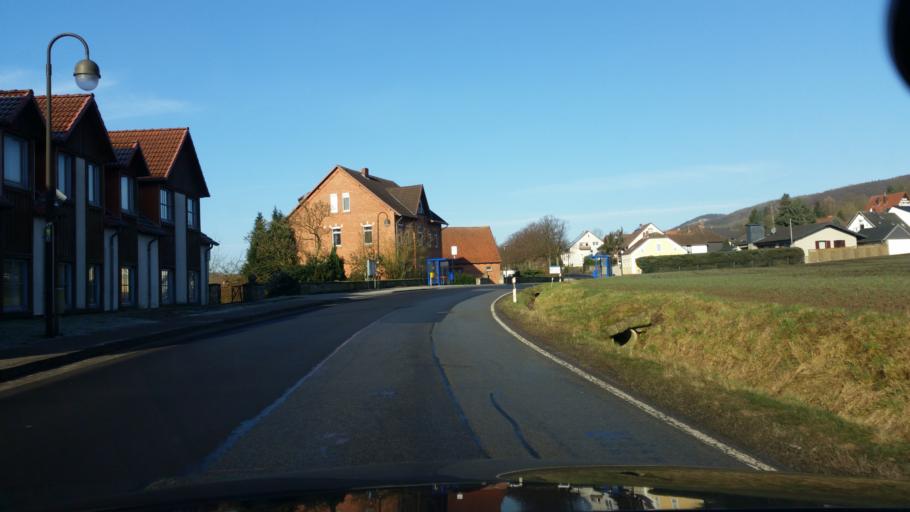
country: DE
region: Lower Saxony
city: Hameln
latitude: 52.1475
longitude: 9.3997
